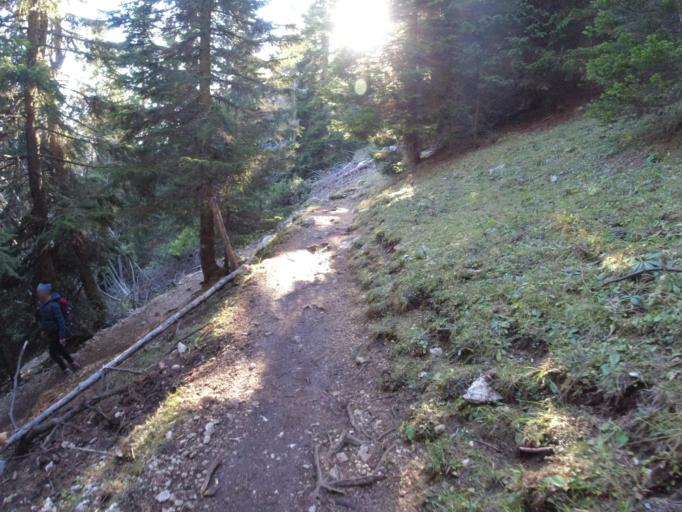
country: AT
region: Carinthia
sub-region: Politischer Bezirk Volkermarkt
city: Gallizien
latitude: 46.5030
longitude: 14.5056
